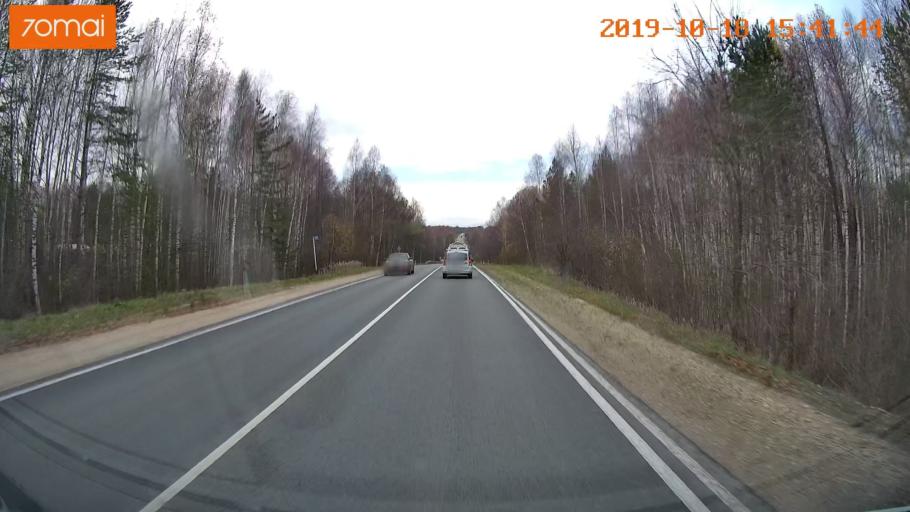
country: RU
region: Vladimir
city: Golovino
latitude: 55.9487
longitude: 40.5786
